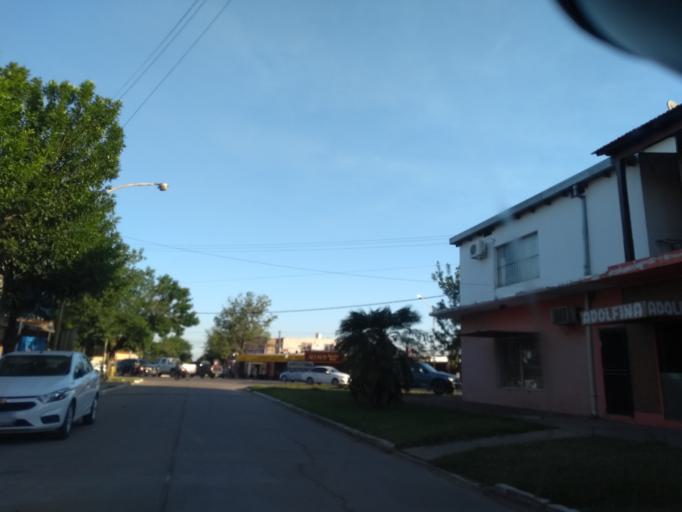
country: AR
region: Chaco
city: Barranqueras
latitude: -27.4826
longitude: -58.9458
